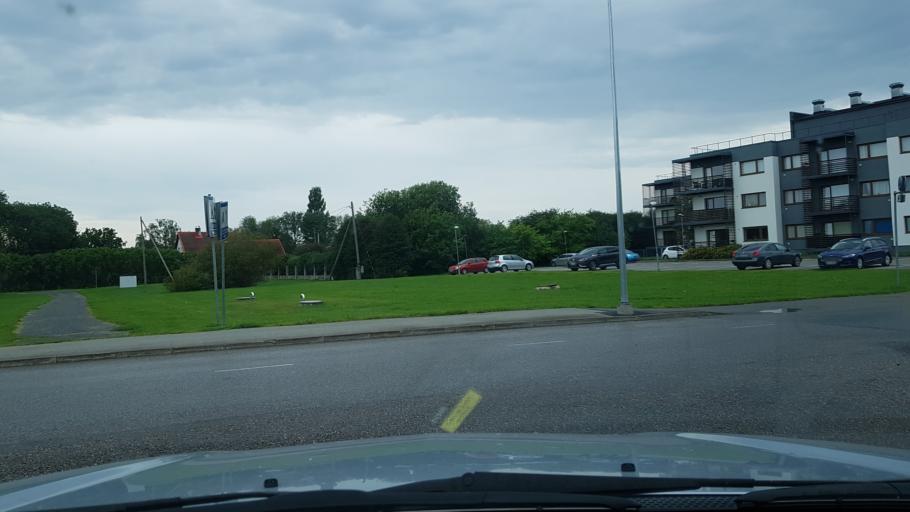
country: EE
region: Harju
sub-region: Rae vald
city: Jueri
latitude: 59.3531
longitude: 24.9085
